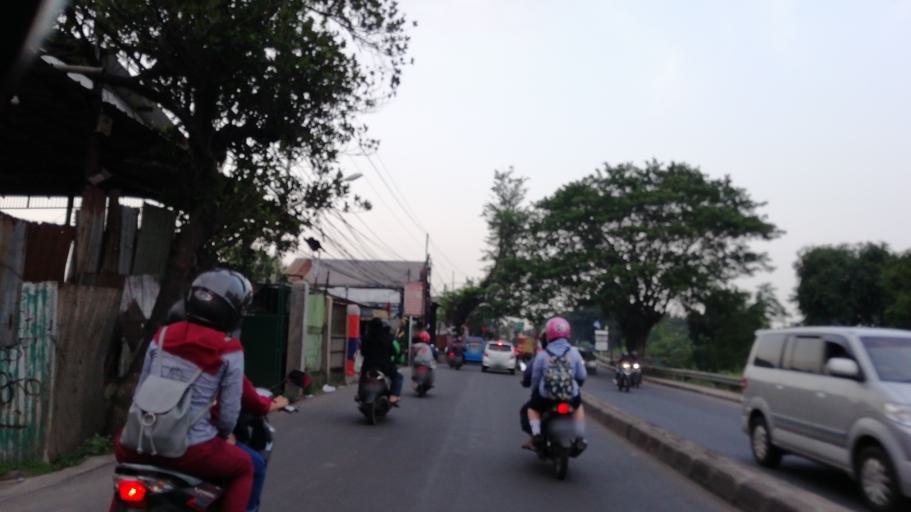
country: ID
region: West Java
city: Cibinong
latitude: -6.4491
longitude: 106.8532
